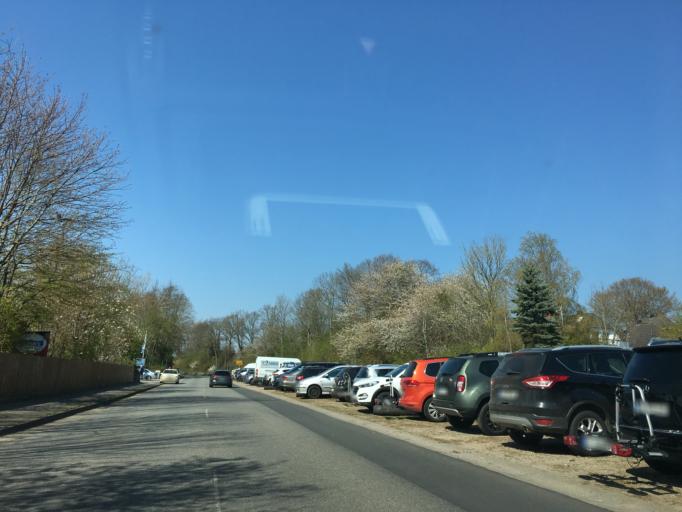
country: DE
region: Schleswig-Holstein
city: Dollrottfeld
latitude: 54.5860
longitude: 9.8173
